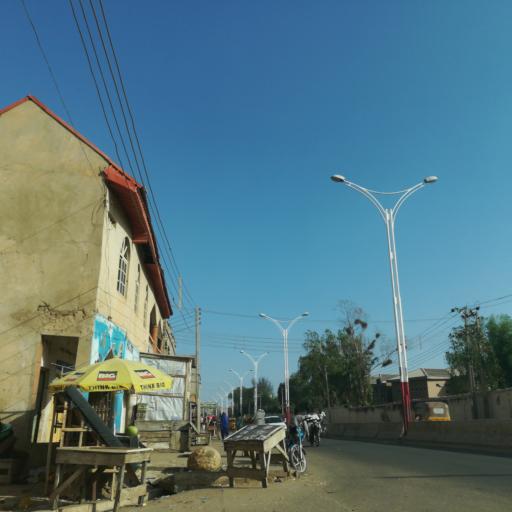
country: NG
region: Kano
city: Kano
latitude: 12.0152
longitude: 8.4974
